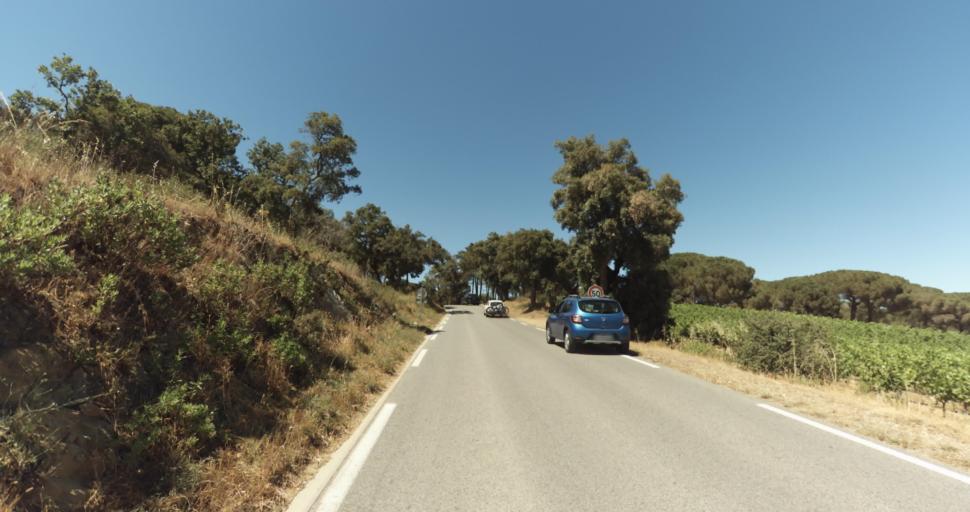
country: FR
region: Provence-Alpes-Cote d'Azur
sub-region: Departement du Var
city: Gassin
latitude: 43.2406
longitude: 6.5631
